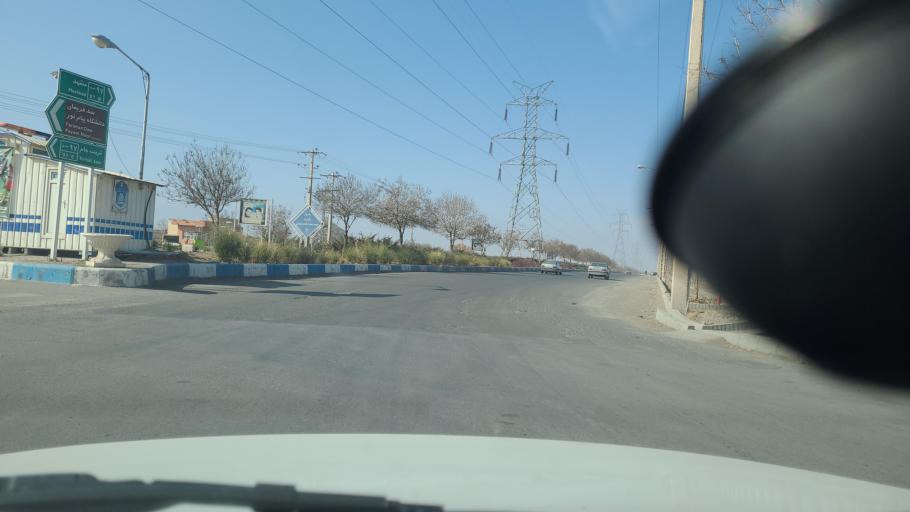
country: IR
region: Razavi Khorasan
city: Fariman
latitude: 35.6949
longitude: 59.8441
